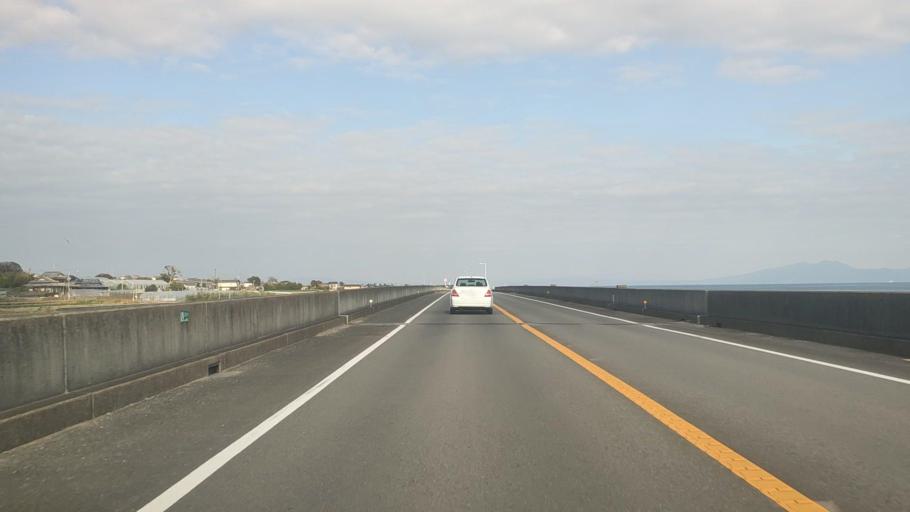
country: JP
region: Nagasaki
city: Shimabara
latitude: 32.7236
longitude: 130.3608
